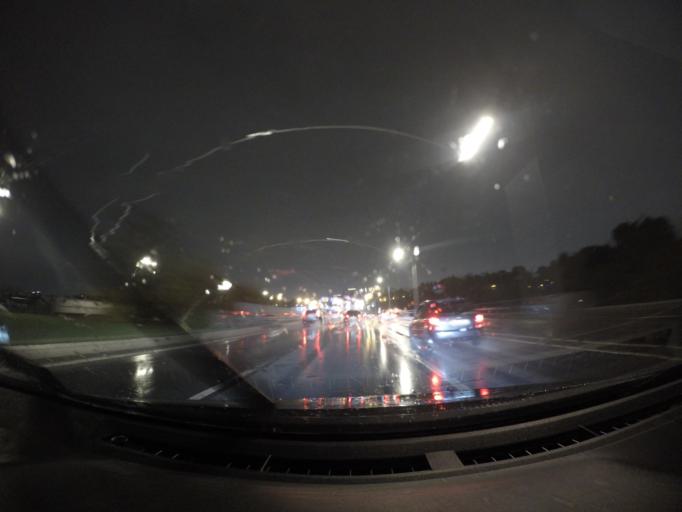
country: RU
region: Moskovskaya
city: Kur'yanovo
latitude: 55.6306
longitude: 37.7060
